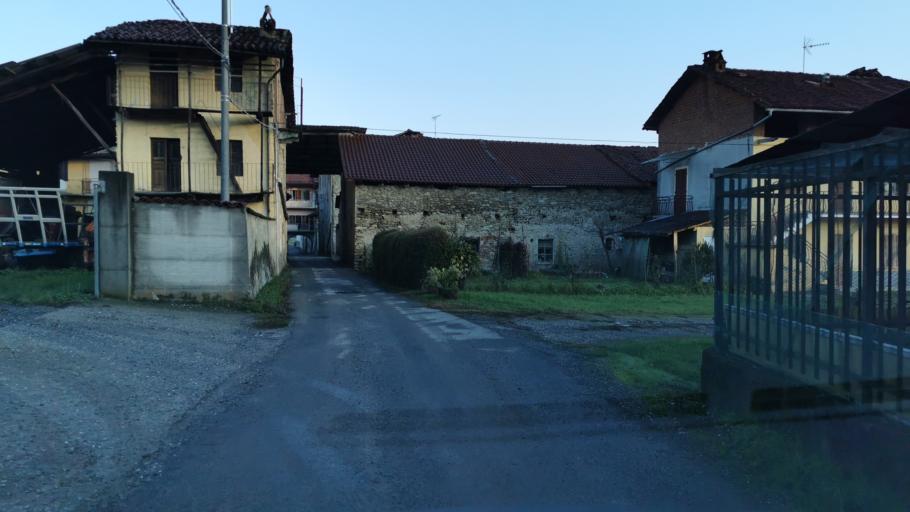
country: IT
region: Piedmont
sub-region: Provincia di Torino
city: Levone
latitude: 45.3007
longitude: 7.6017
